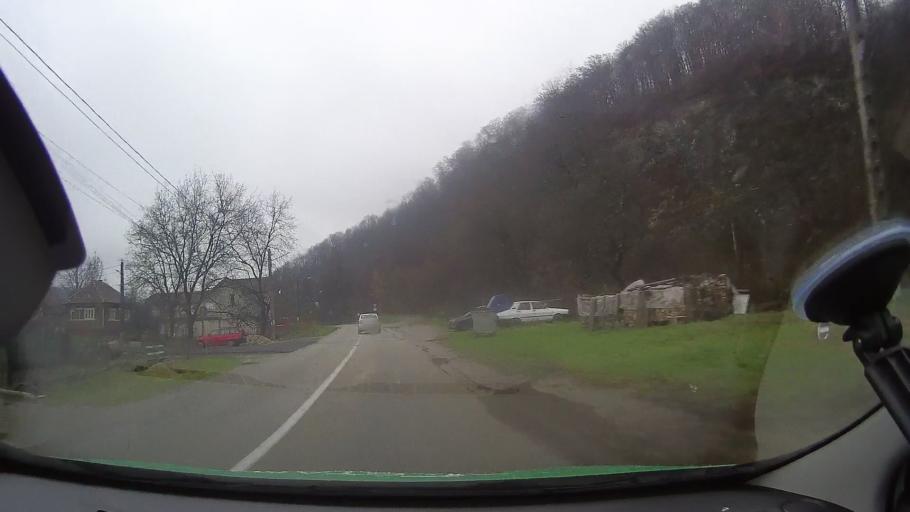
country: RO
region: Arad
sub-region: Comuna Moneasa
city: Moneasa
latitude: 46.4380
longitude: 22.2476
